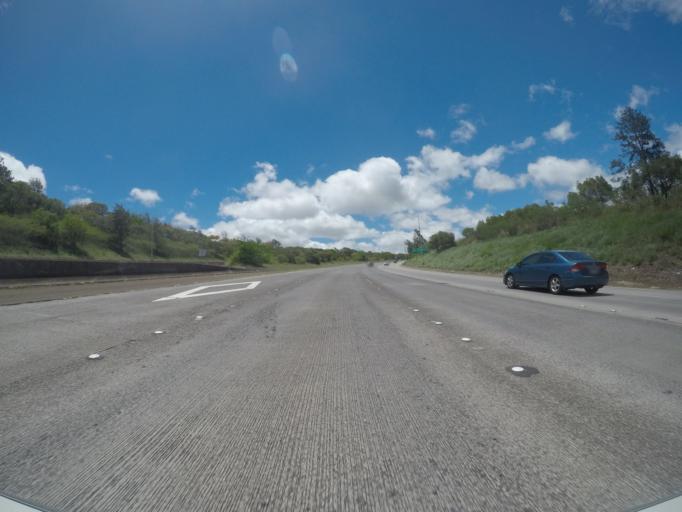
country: US
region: Hawaii
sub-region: Honolulu County
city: Waipio
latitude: 21.4163
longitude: -157.9929
